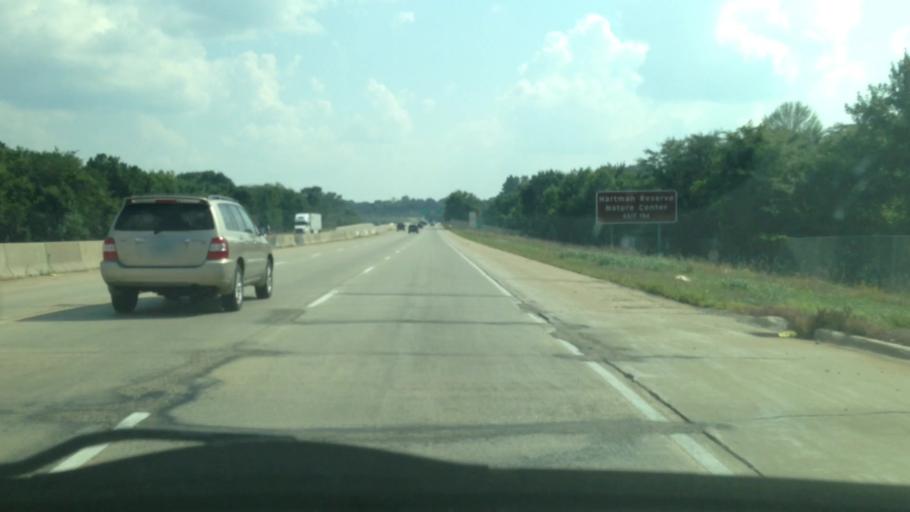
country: US
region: Iowa
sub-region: Black Hawk County
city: Cedar Falls
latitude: 42.5249
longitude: -92.3893
